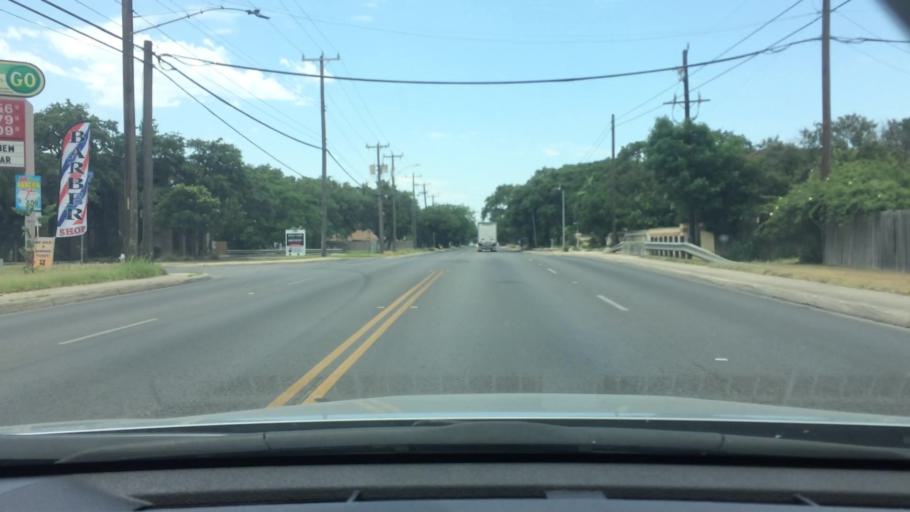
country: US
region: Texas
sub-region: Bexar County
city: Hollywood Park
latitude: 29.5730
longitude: -98.4473
